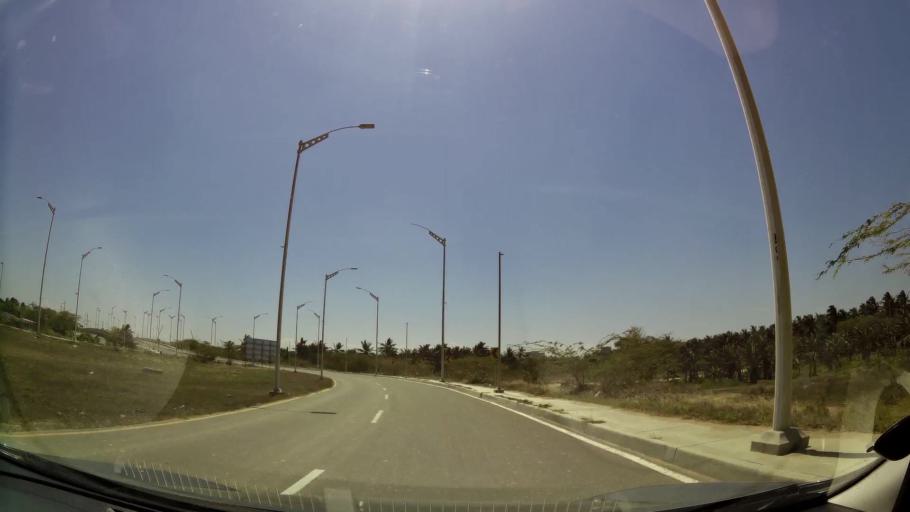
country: CO
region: Atlantico
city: Barranquilla
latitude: 10.9909
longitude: -74.7720
